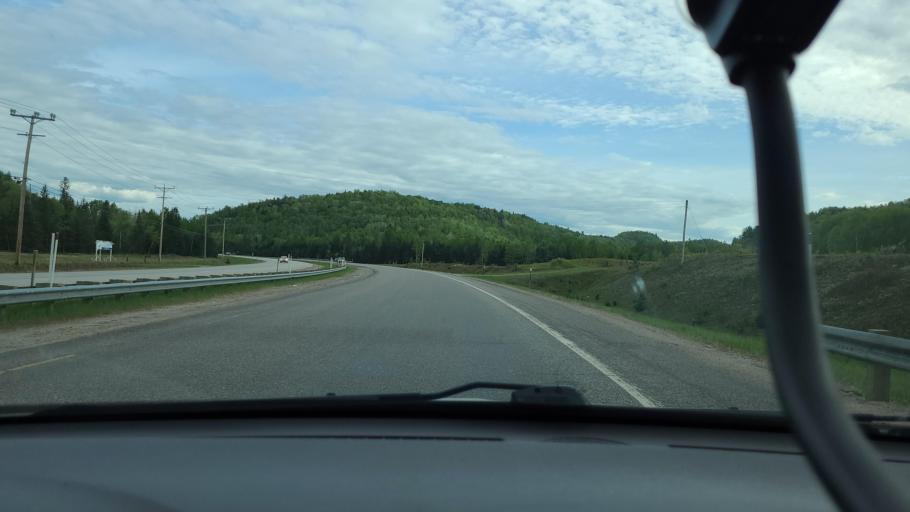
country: CA
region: Quebec
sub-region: Laurentides
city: Labelle
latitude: 46.2317
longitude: -74.7160
